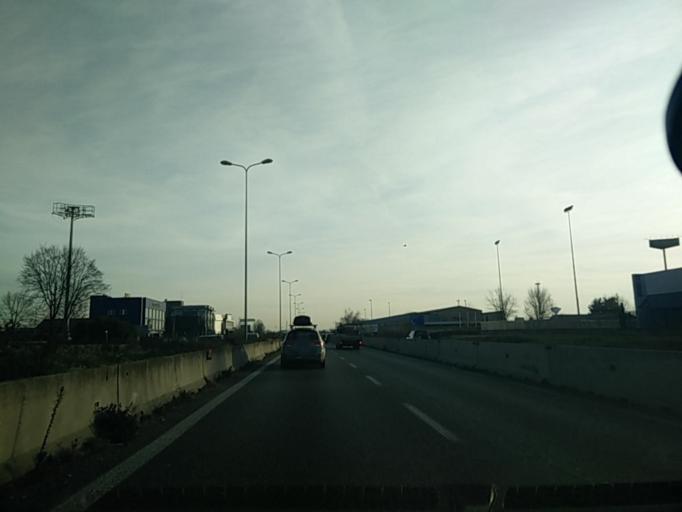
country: IT
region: Lombardy
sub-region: Provincia di Monza e Brianza
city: Varedo
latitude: 45.5949
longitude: 9.1724
